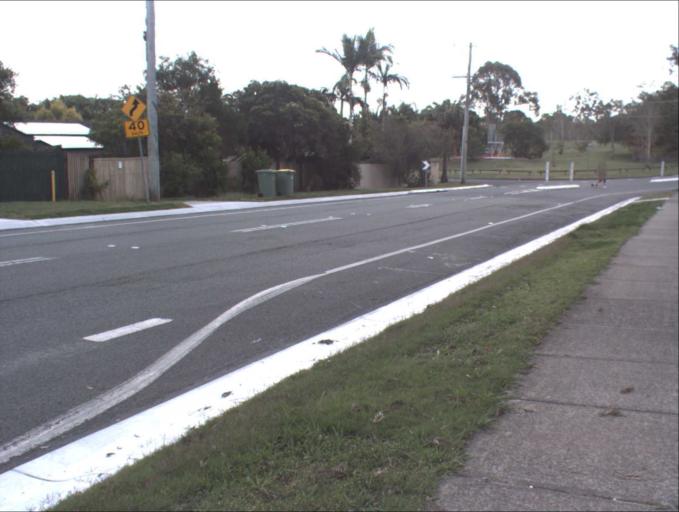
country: AU
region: Queensland
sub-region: Logan
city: Waterford West
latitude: -27.6915
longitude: 153.1509
